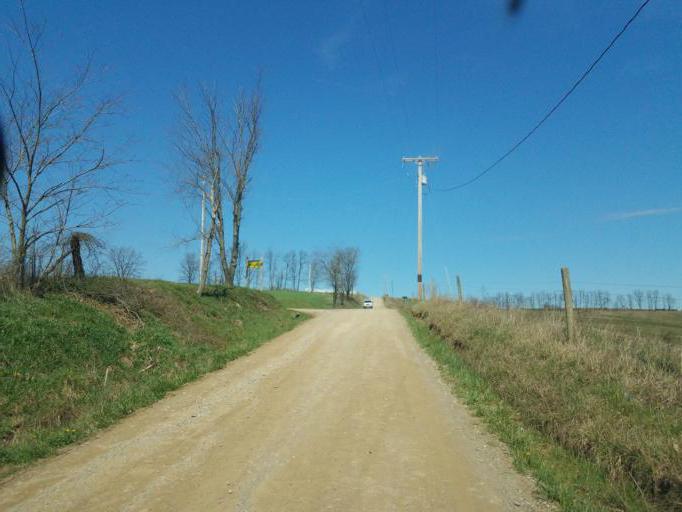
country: US
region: Ohio
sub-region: Knox County
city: Oak Hill
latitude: 40.3312
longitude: -82.1910
